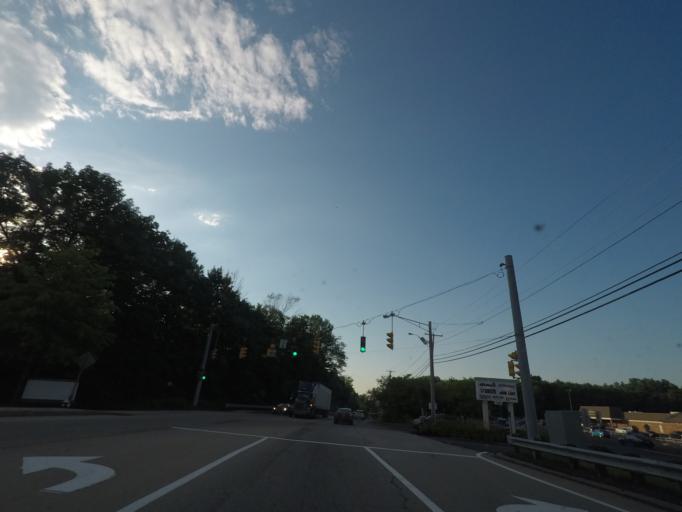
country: US
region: Massachusetts
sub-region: Worcester County
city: Sturbridge
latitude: 42.0968
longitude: -72.0722
